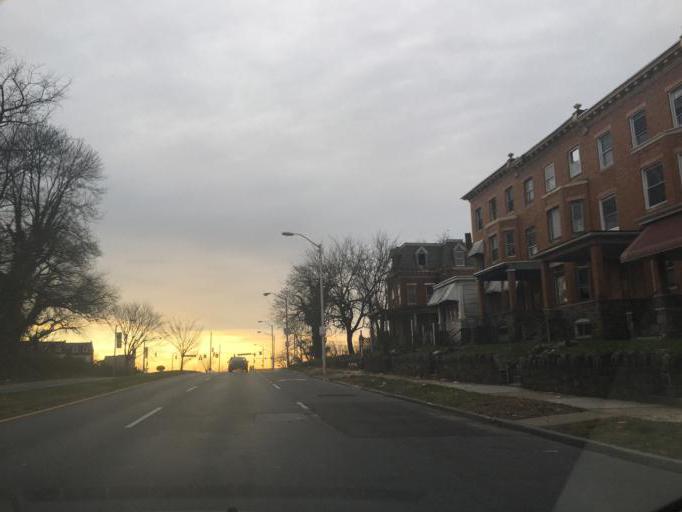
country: US
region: Maryland
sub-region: City of Baltimore
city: Baltimore
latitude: 39.3198
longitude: -76.6536
